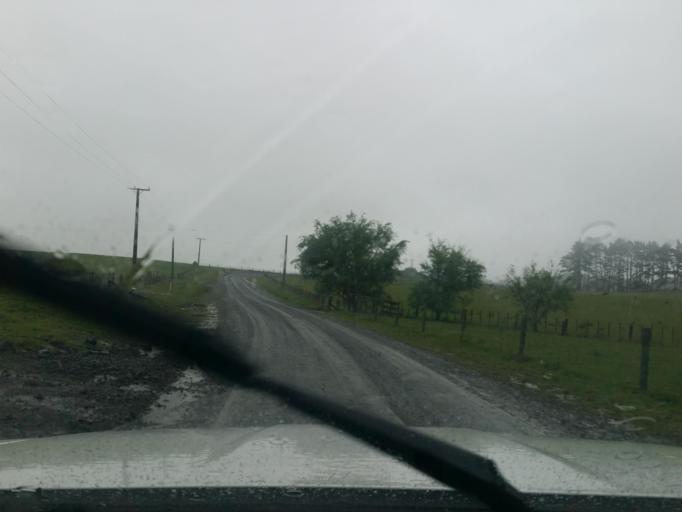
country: NZ
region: Northland
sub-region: Whangarei
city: Maungatapere
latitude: -35.8025
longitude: 174.0497
